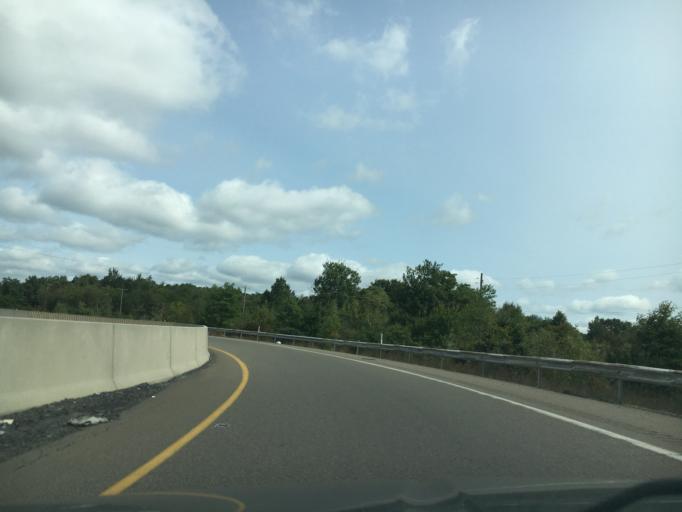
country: US
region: Pennsylvania
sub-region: Schuylkill County
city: McAdoo
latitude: 40.8802
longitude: -76.0004
